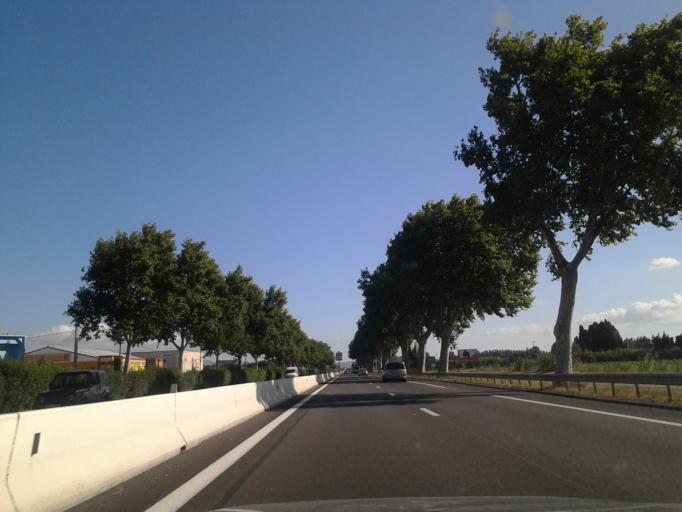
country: FR
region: Languedoc-Roussillon
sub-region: Departement des Pyrenees-Orientales
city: Rivesaltes
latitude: 42.7622
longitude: 2.8982
